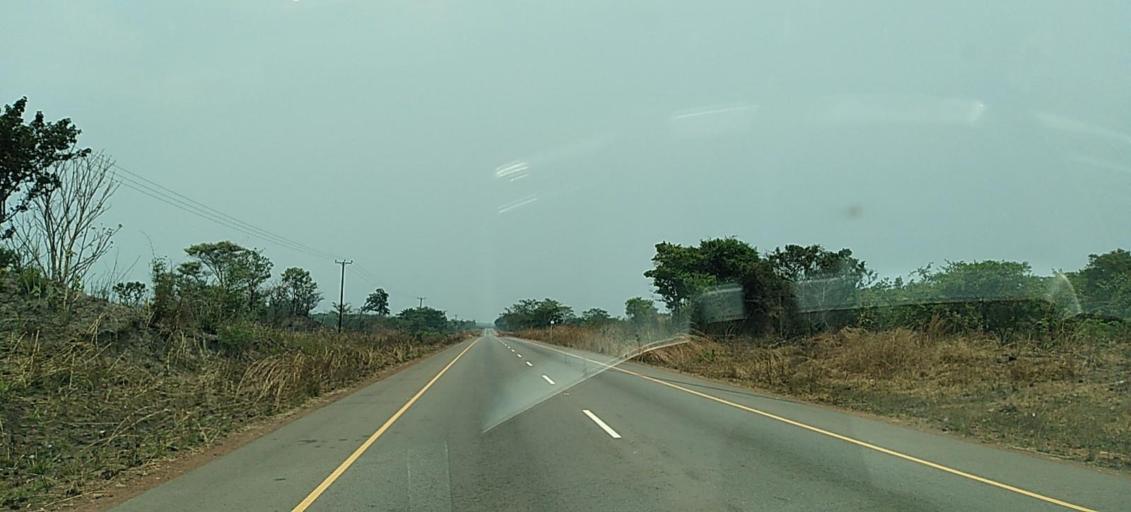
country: ZM
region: Copperbelt
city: Chililabombwe
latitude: -12.4000
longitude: 27.3739
